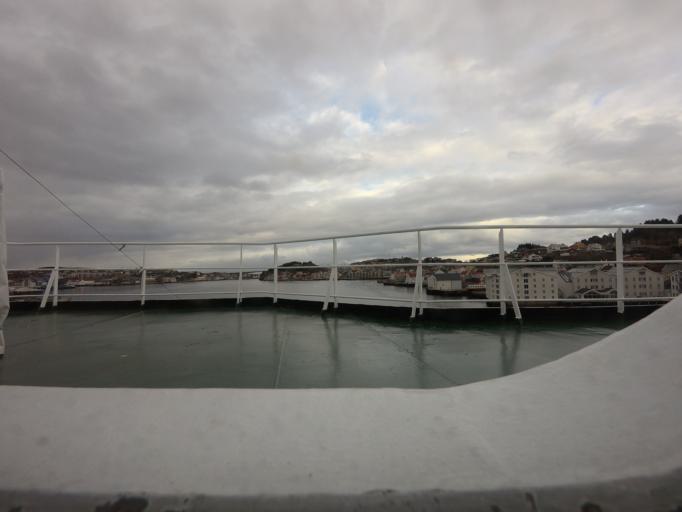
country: NO
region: More og Romsdal
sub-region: Kristiansund
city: Kristiansund
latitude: 63.1077
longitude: 7.7317
